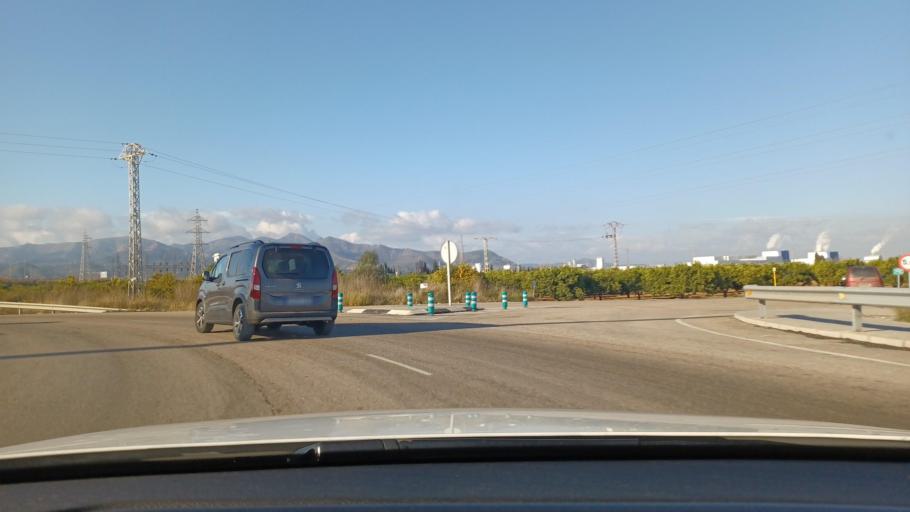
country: ES
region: Valencia
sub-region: Provincia de Castello
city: Moncofar
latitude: 39.8137
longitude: -0.1608
